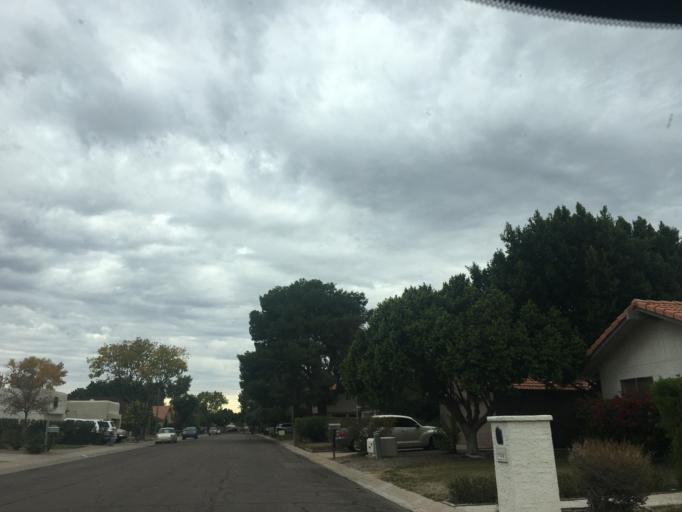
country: US
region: Arizona
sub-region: Maricopa County
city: Guadalupe
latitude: 33.3746
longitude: -111.9261
